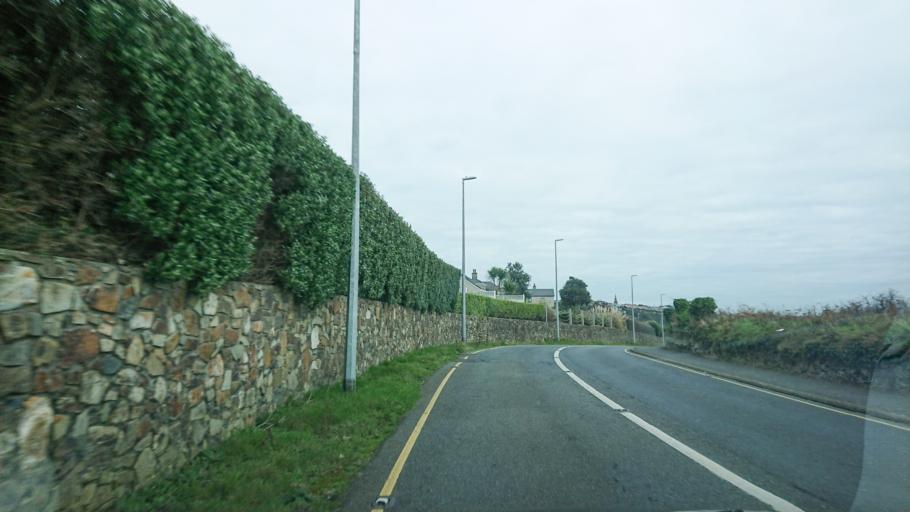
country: IE
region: Munster
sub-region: Waterford
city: Tra Mhor
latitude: 52.1488
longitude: -7.1638
